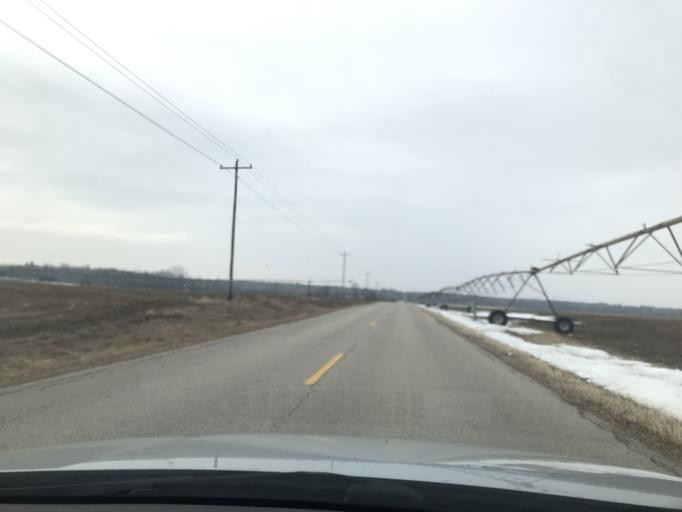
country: US
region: Wisconsin
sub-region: Oconto County
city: Oconto Falls
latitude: 44.8491
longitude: -88.1676
